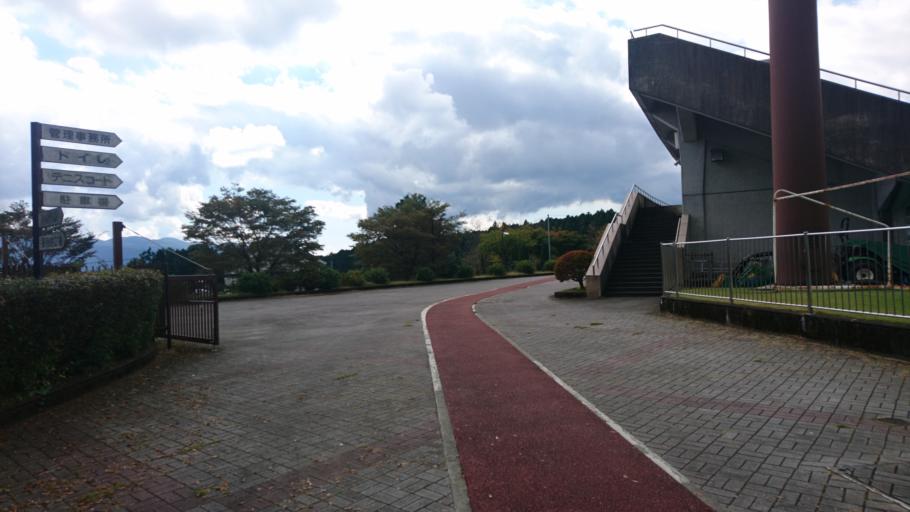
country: JP
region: Shizuoka
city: Gotemba
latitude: 35.3139
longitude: 138.9121
